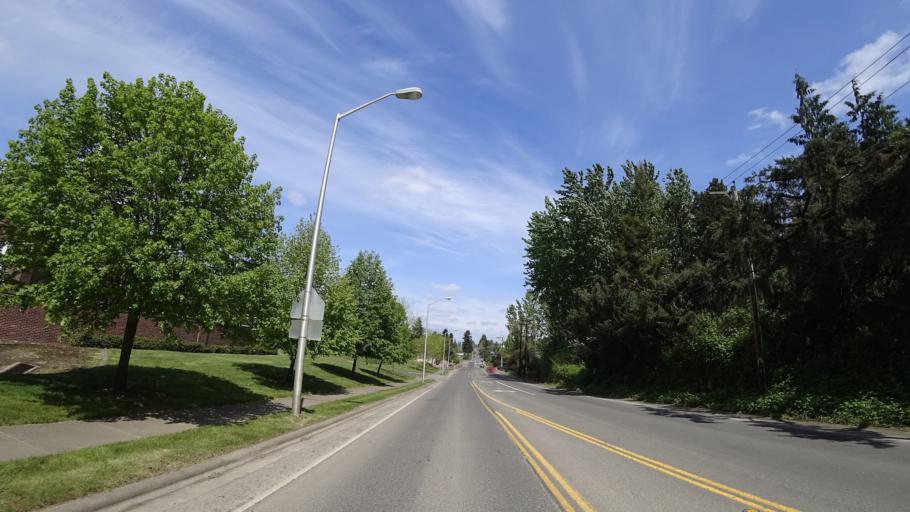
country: US
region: Oregon
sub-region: Washington County
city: Aloha
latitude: 45.4820
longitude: -122.8936
